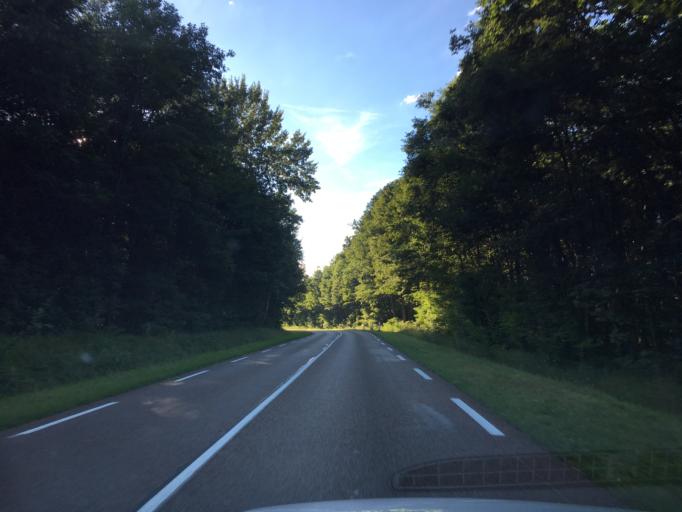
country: FR
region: Bourgogne
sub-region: Departement de l'Yonne
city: Charbuy
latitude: 47.8115
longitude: 3.4836
